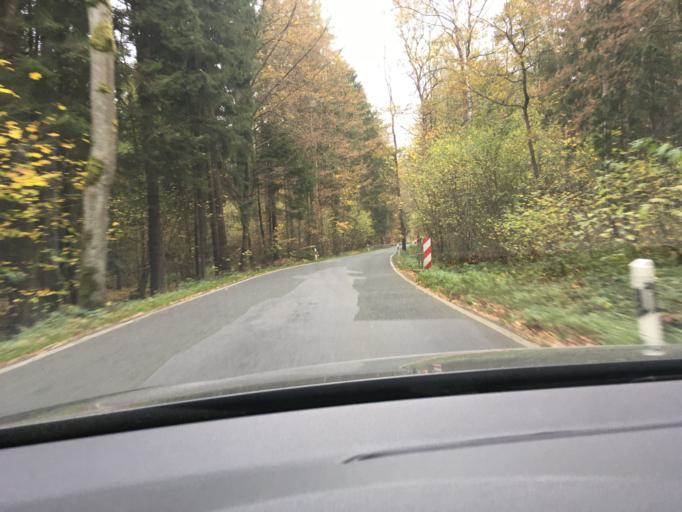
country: DE
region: Saxony
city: Reinhardtsgrimma
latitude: 50.8912
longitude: 13.7963
